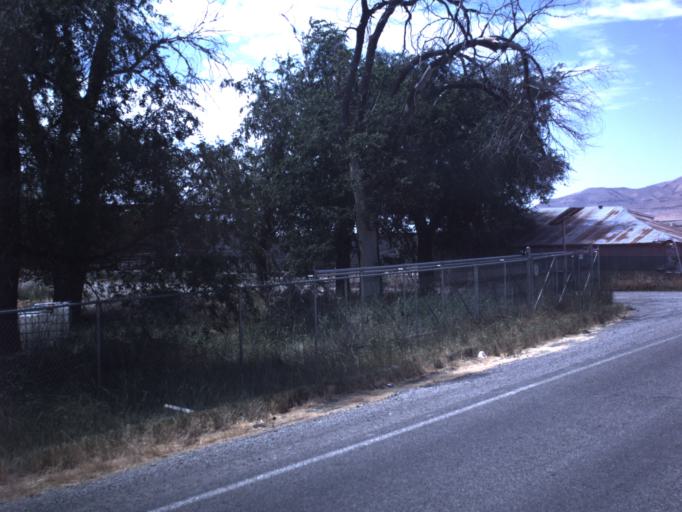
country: US
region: Utah
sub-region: Box Elder County
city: Tremonton
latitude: 41.7107
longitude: -112.2105
